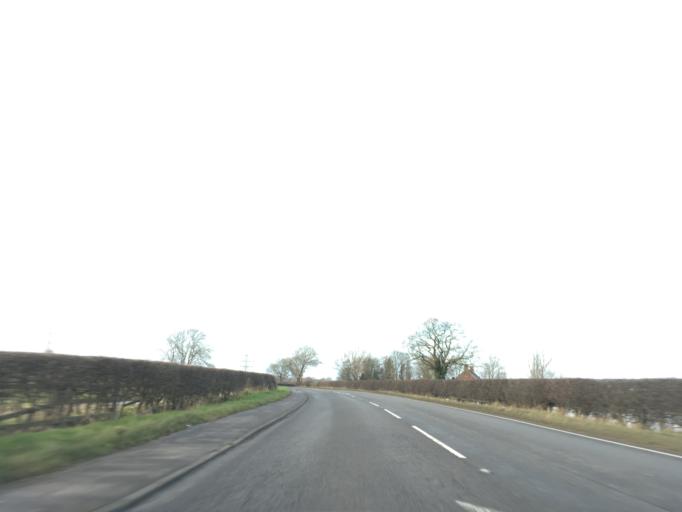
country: GB
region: England
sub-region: Nottinghamshire
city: South Collingham
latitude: 53.1619
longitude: -0.7628
